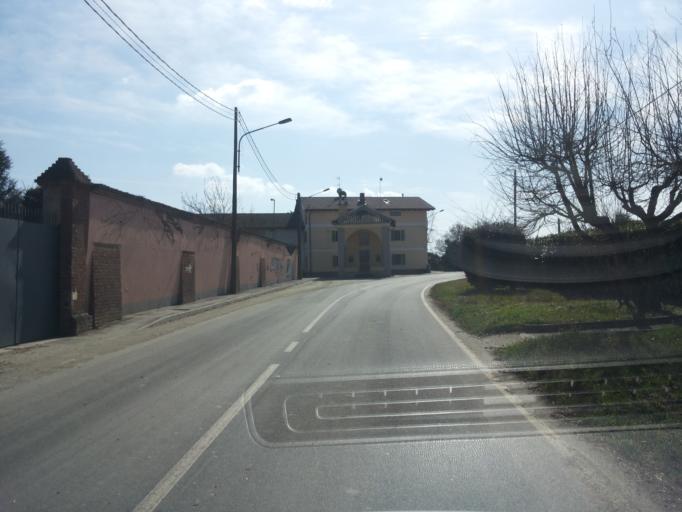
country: IT
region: Piedmont
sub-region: Provincia di Vercelli
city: Asigliano Vercellese
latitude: 45.2585
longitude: 8.4009
